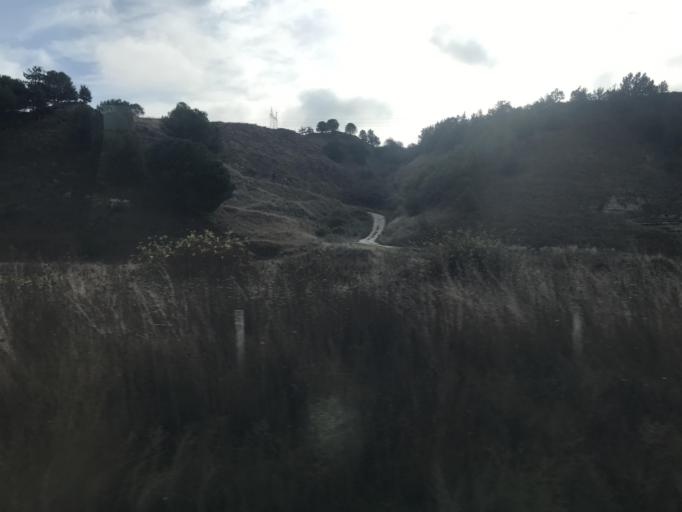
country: ES
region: Castille and Leon
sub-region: Provincia de Burgos
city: Pradanos de Bureba
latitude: 42.5050
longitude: -3.3438
